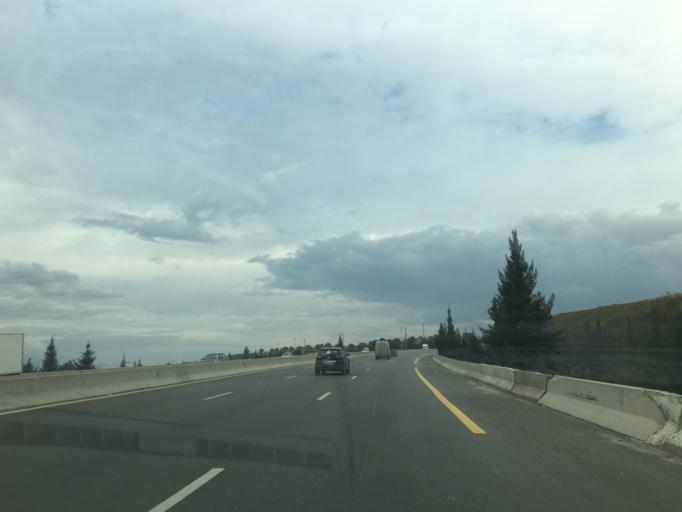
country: DZ
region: Bouira
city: Bouira
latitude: 36.3125
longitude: 4.0547
